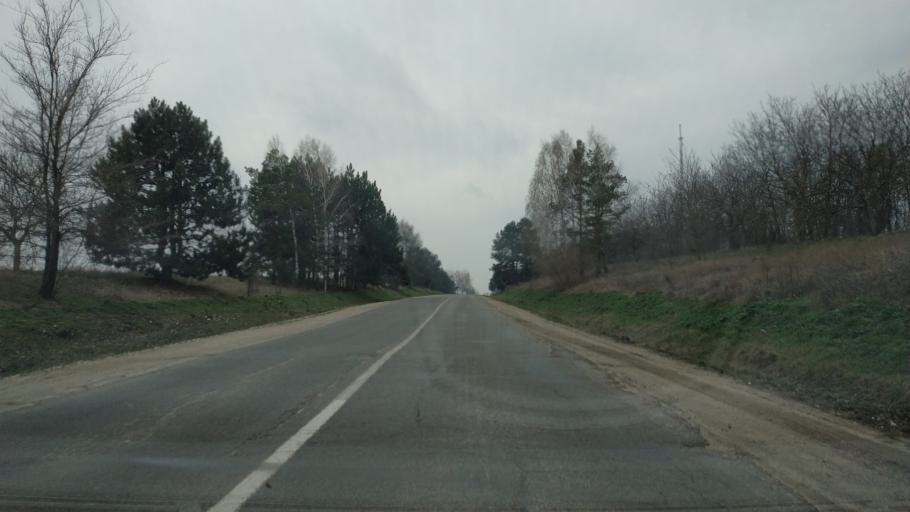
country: MD
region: Cahul
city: Cahul
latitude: 45.9382
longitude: 28.2880
